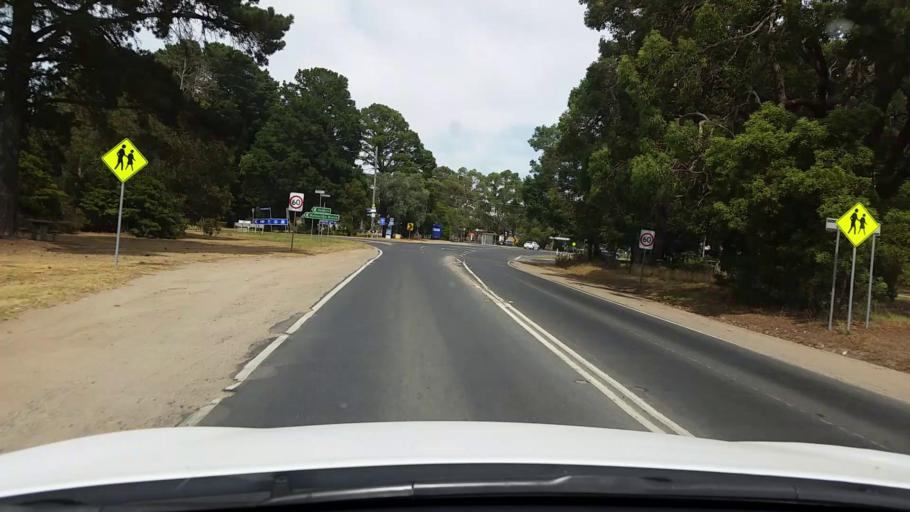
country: AU
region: Victoria
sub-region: Mornington Peninsula
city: Balnarring
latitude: -38.3732
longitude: 145.1280
